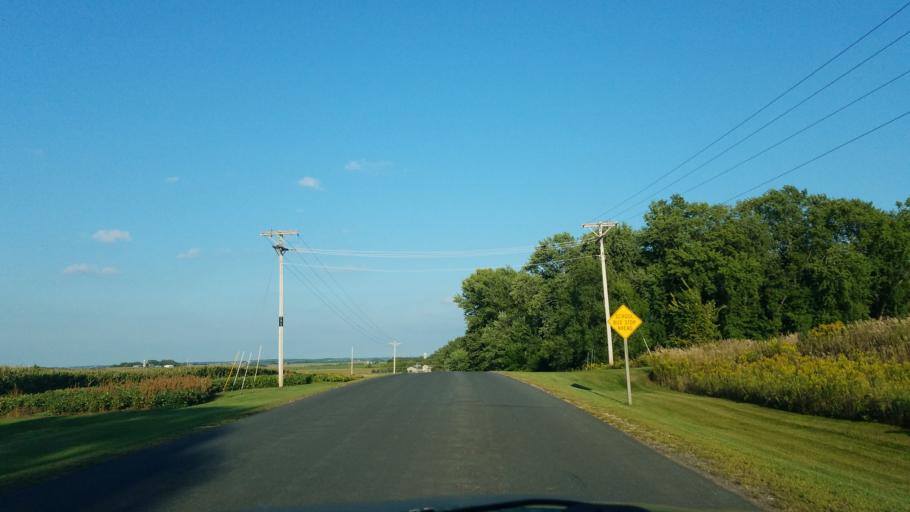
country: US
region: Wisconsin
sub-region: Saint Croix County
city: Roberts
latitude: 45.0072
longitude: -92.5422
